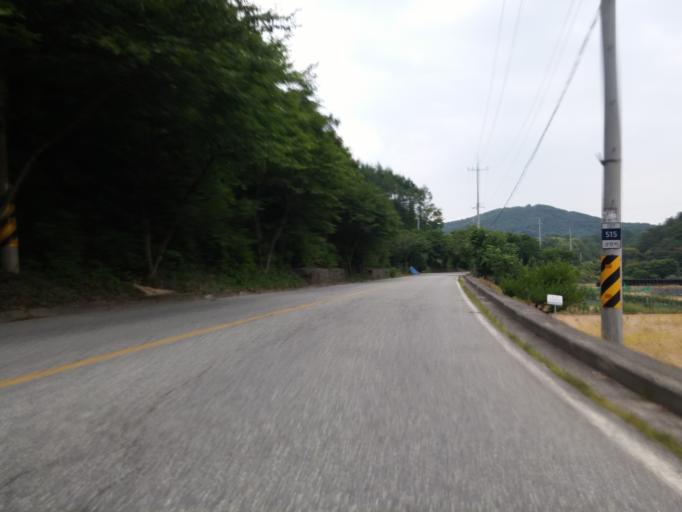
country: KR
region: Chungcheongbuk-do
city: Okcheon
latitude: 36.1950
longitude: 127.5619
